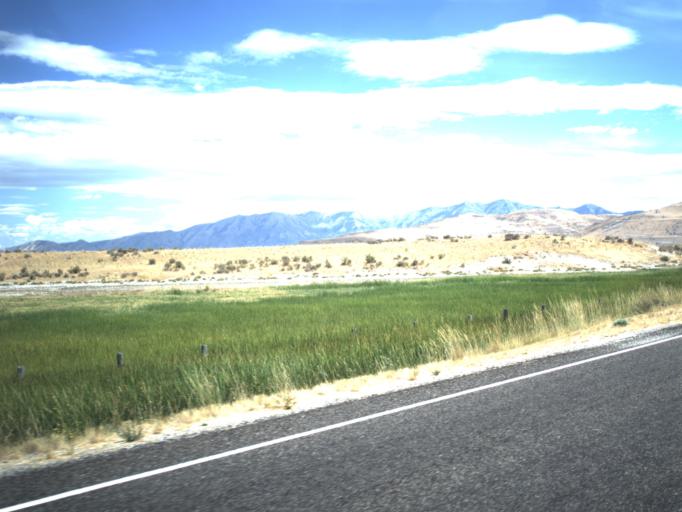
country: US
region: Utah
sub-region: Box Elder County
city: Tremonton
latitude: 41.6078
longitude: -112.3266
